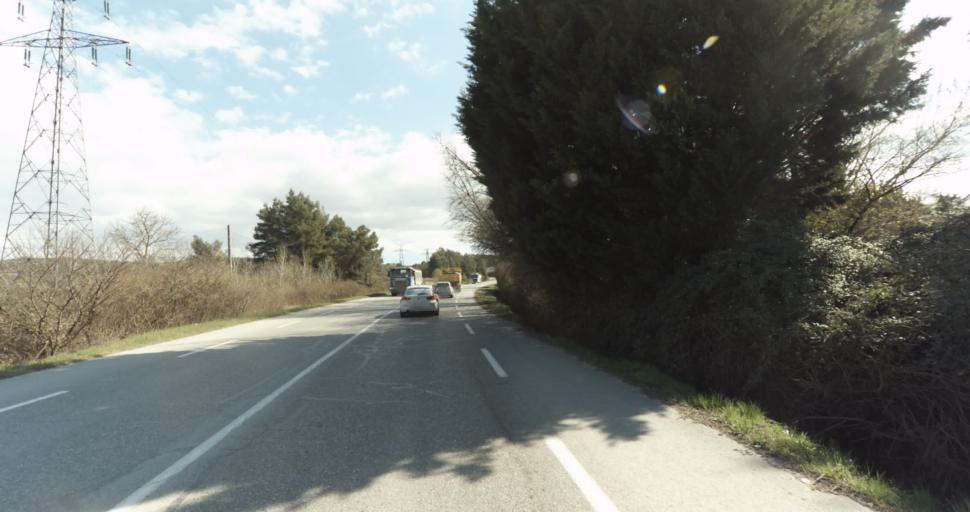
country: FR
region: Provence-Alpes-Cote d'Azur
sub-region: Departement des Bouches-du-Rhone
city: Gardanne
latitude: 43.4623
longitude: 5.4878
